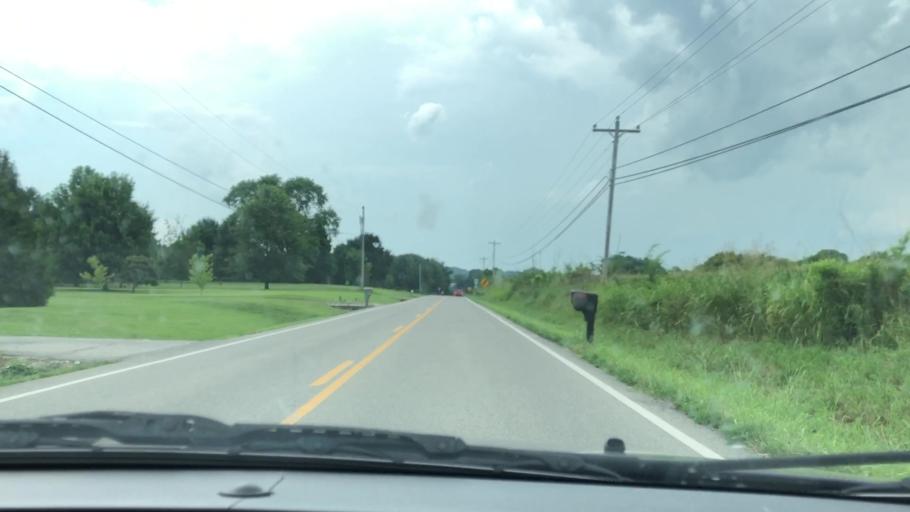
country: US
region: Tennessee
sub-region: Maury County
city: Spring Hill
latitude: 35.7721
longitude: -87.0060
